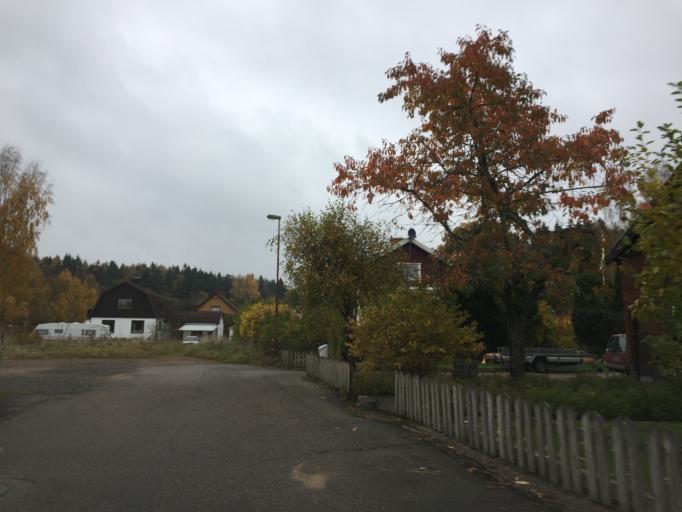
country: SE
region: Vaestra Goetaland
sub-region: Trollhattan
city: Sjuntorp
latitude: 58.2035
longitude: 12.2401
